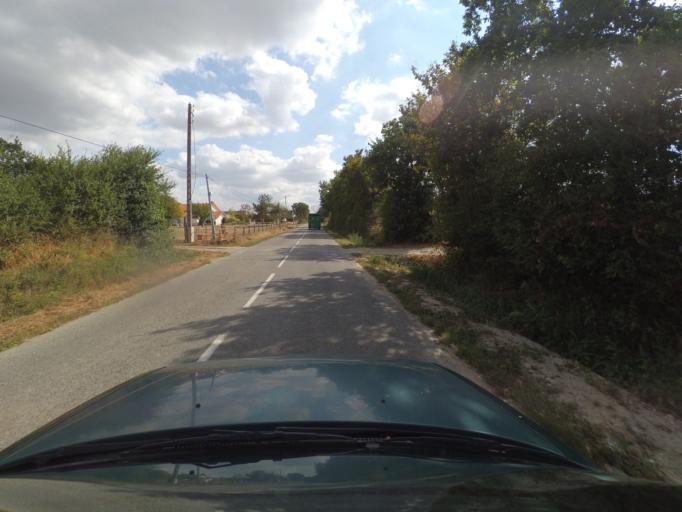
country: FR
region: Pays de la Loire
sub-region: Departement de la Loire-Atlantique
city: La Planche
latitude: 47.0249
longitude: -1.4212
